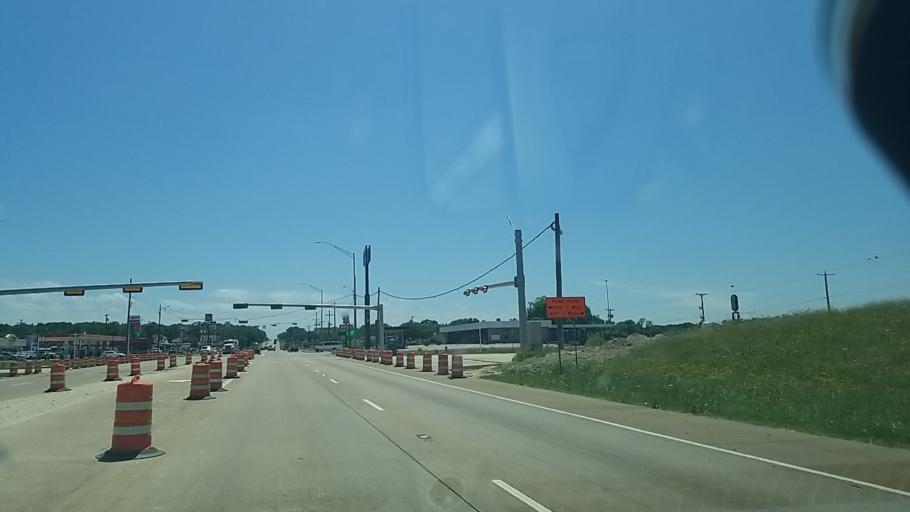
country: US
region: Texas
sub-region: Leon County
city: Buffalo
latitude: 31.4506
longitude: -96.0765
